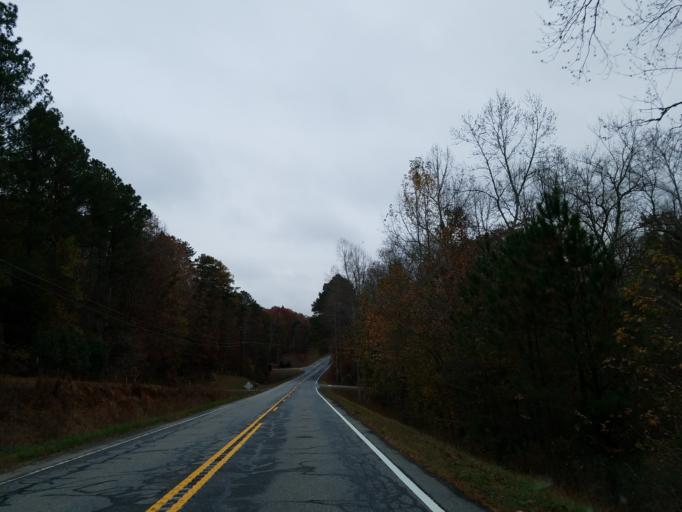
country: US
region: Georgia
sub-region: Cherokee County
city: Canton
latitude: 34.2357
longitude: -84.6199
